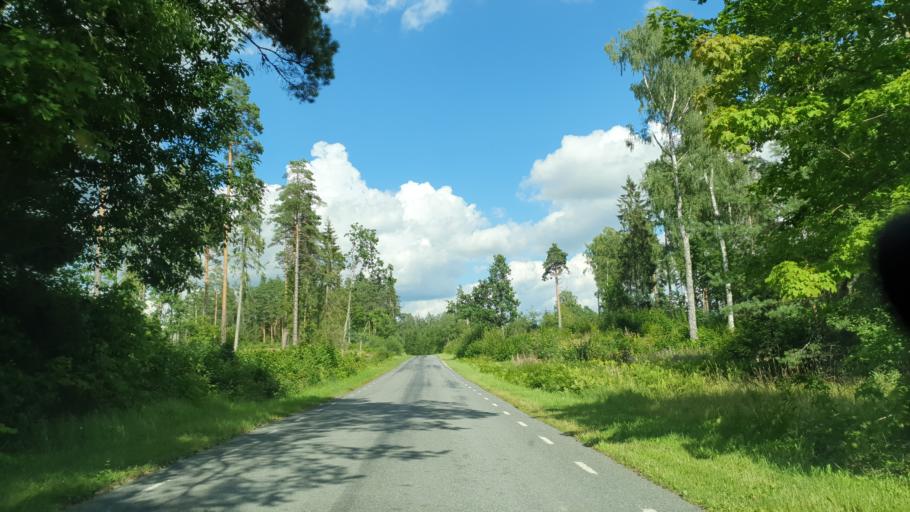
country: EE
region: Jogevamaa
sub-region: Tabivere vald
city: Tabivere
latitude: 58.6314
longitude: 26.5977
